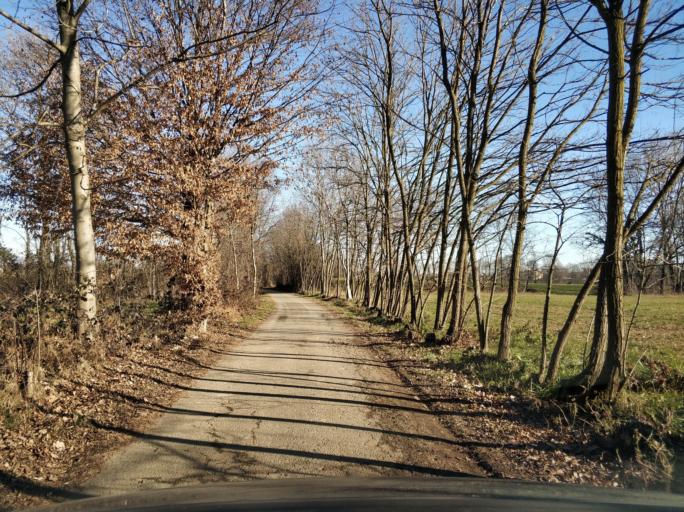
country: IT
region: Piedmont
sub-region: Provincia di Torino
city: San Francesco al Campo
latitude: 45.2347
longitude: 7.6443
